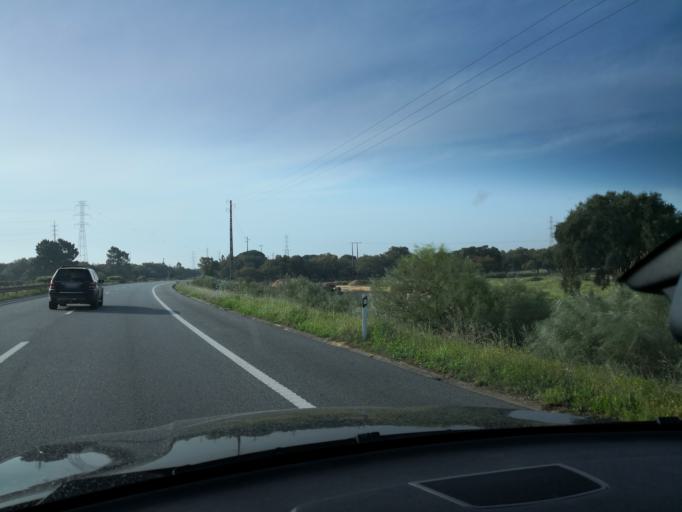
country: PT
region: Setubal
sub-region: Palmela
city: Palmela
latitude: 38.5799
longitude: -8.8703
